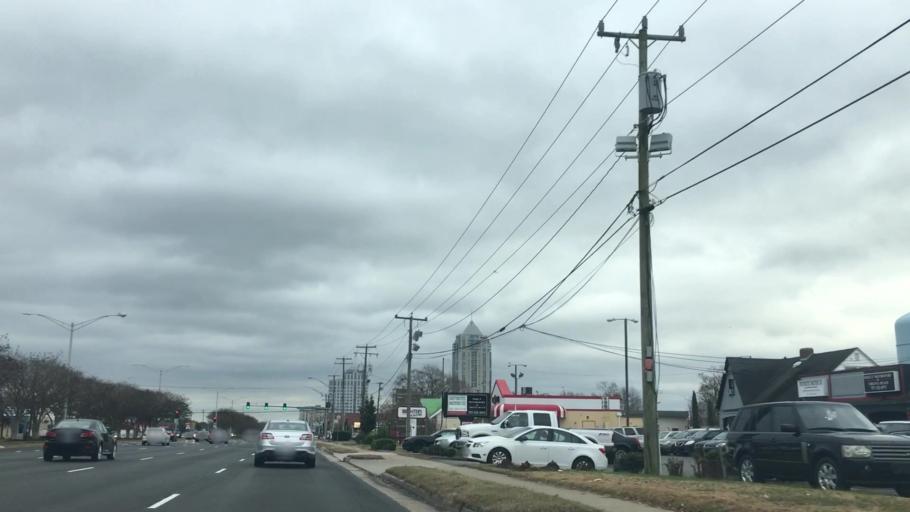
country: US
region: Virginia
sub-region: City of Chesapeake
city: Chesapeake
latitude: 36.8436
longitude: -76.1479
